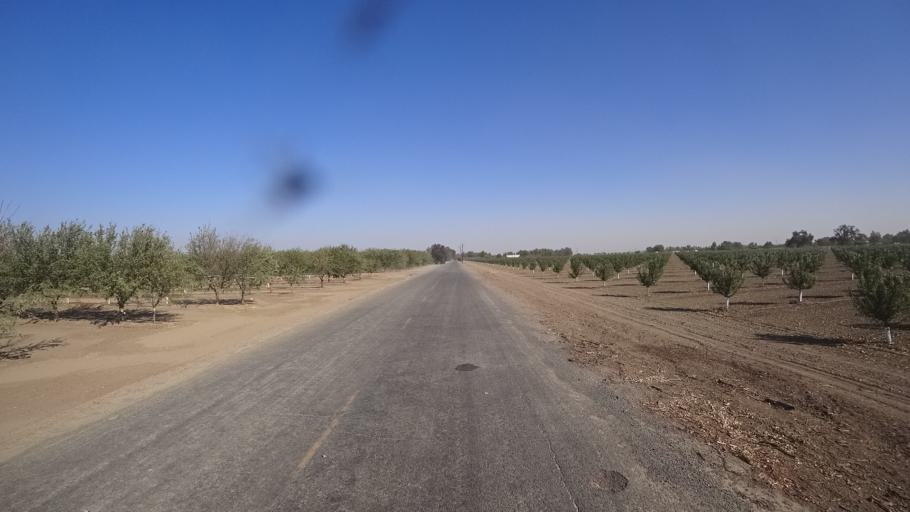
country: US
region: California
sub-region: Yolo County
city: Woodland
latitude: 38.7496
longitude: -121.7858
